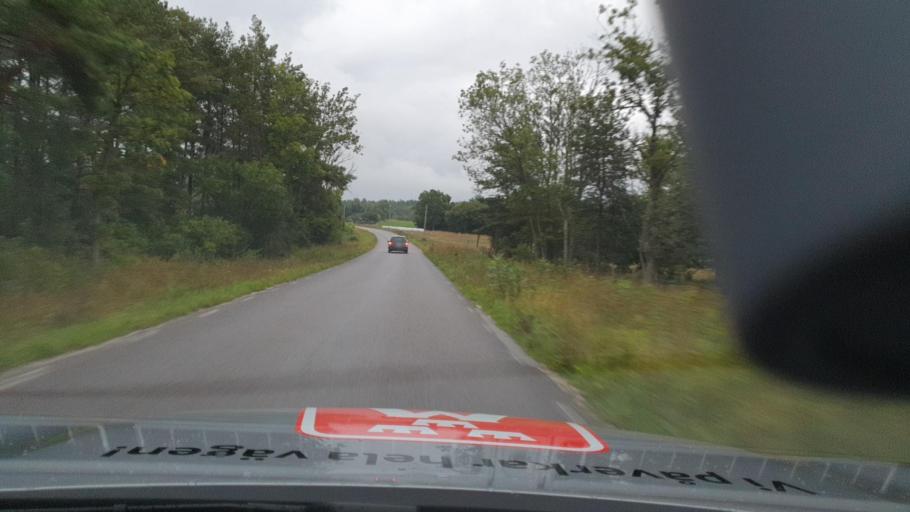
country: SE
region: Gotland
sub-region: Gotland
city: Slite
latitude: 57.7506
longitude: 18.7724
